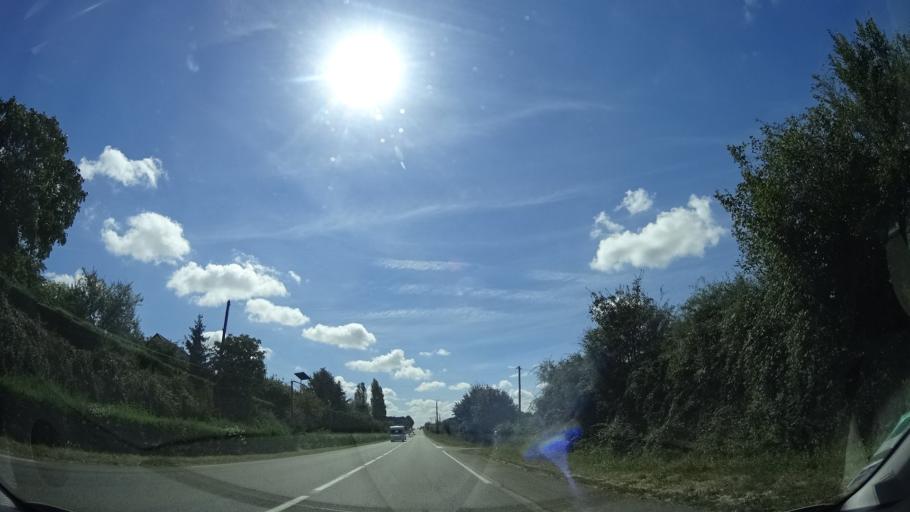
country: FR
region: Pays de la Loire
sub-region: Departement de la Sarthe
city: Auvers-le-Hamon
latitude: 47.8883
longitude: -0.4139
